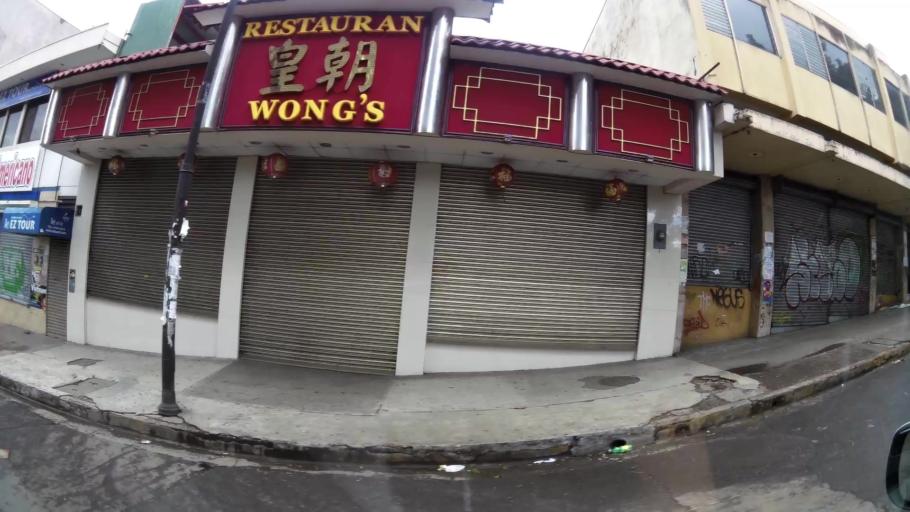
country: CR
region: San Jose
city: San Jose
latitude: 9.9334
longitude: -84.0725
